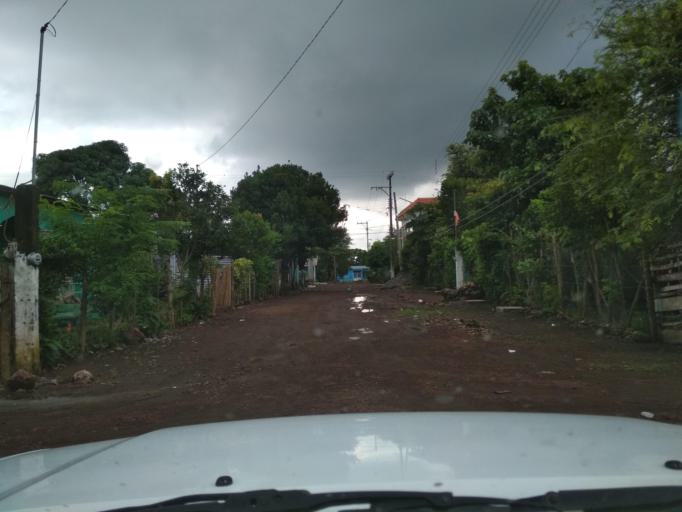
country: MX
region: Veracruz
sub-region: San Andres Tuxtla
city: El Huidero
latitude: 18.3896
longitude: -95.1787
